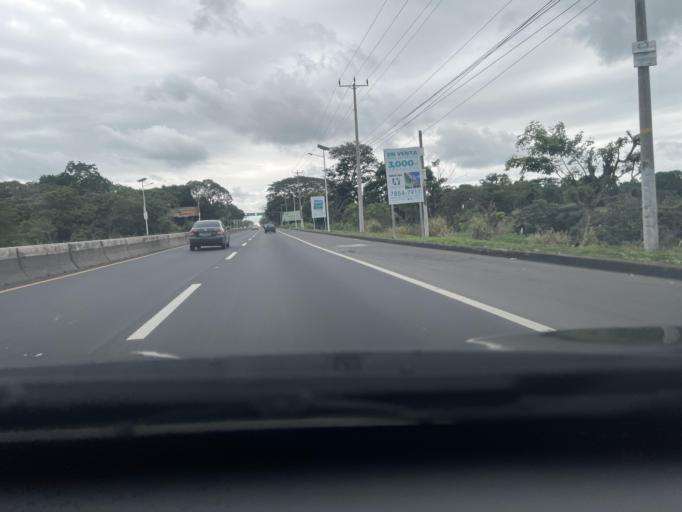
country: SV
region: Santa Ana
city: El Congo
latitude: 13.8917
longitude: -89.4995
